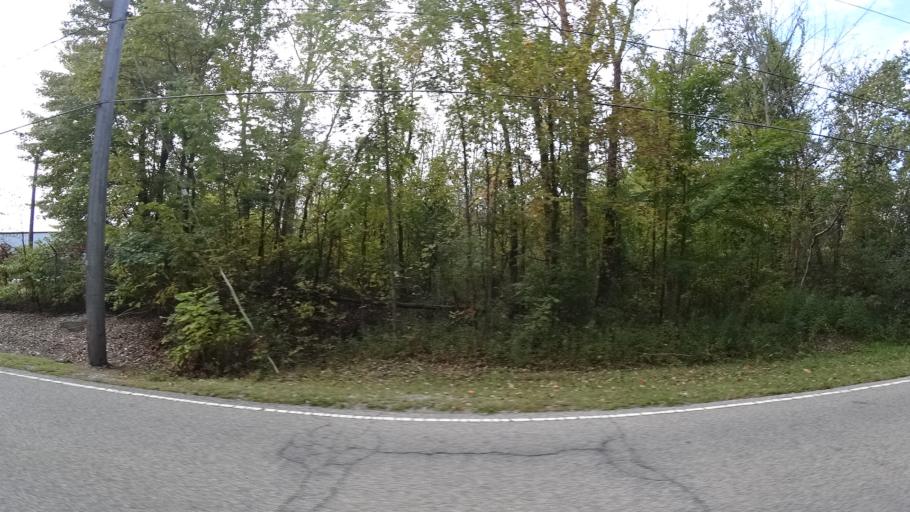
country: US
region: Indiana
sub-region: LaPorte County
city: Long Beach
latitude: 41.7195
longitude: -86.8407
